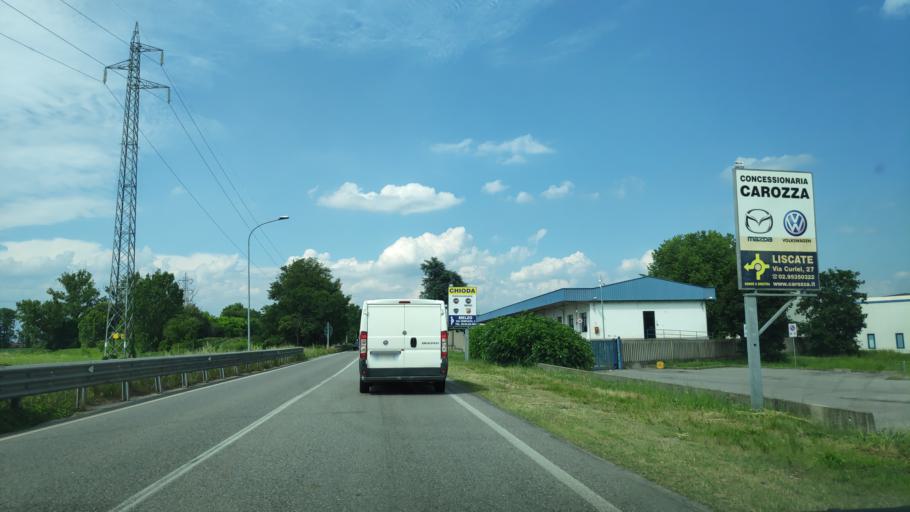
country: IT
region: Lombardy
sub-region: Citta metropolitana di Milano
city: Liscate
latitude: 45.4752
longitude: 9.4236
